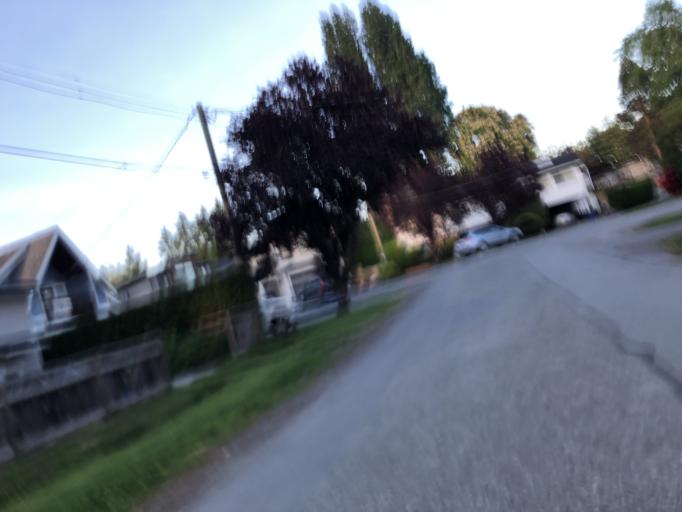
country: CA
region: British Columbia
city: Richmond
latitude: 49.1390
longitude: -123.1321
